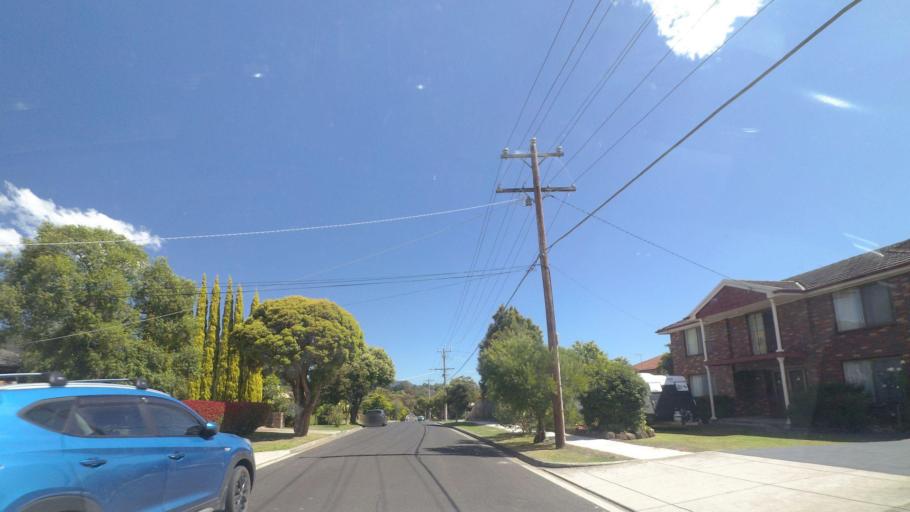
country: AU
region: Victoria
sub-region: Yarra Ranges
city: Kilsyth
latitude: -37.8010
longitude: 145.3303
